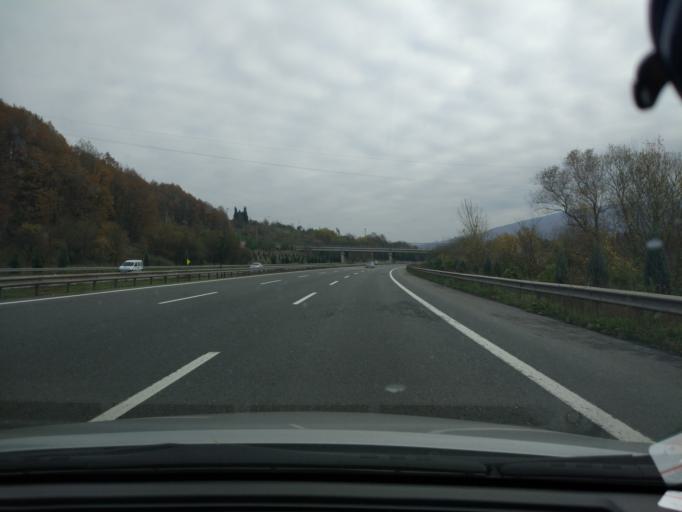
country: TR
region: Sakarya
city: Hendek
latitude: 40.7697
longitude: 30.7672
